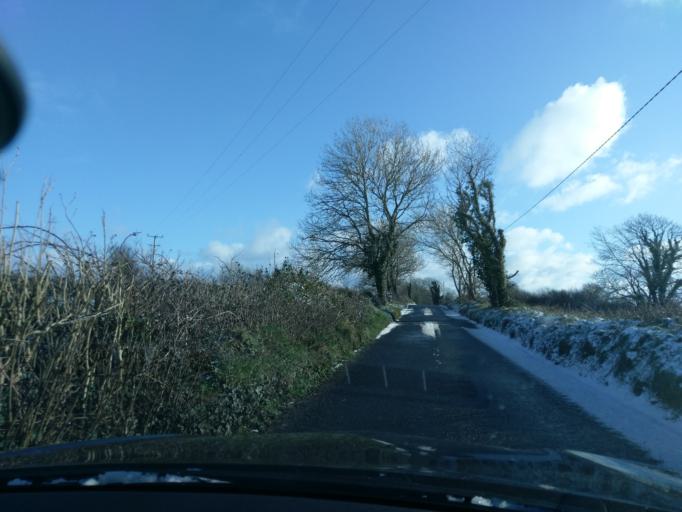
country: IE
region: Connaught
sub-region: County Galway
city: Oranmore
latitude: 53.2020
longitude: -8.8311
